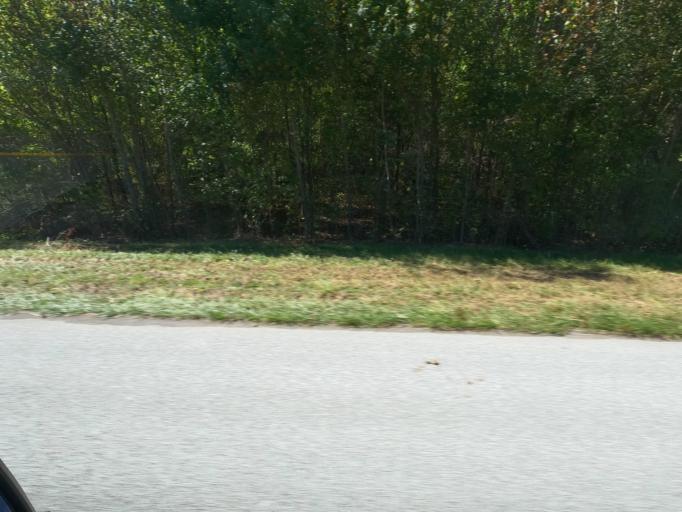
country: US
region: Tennessee
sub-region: Maury County
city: Mount Pleasant
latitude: 35.3942
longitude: -87.2777
